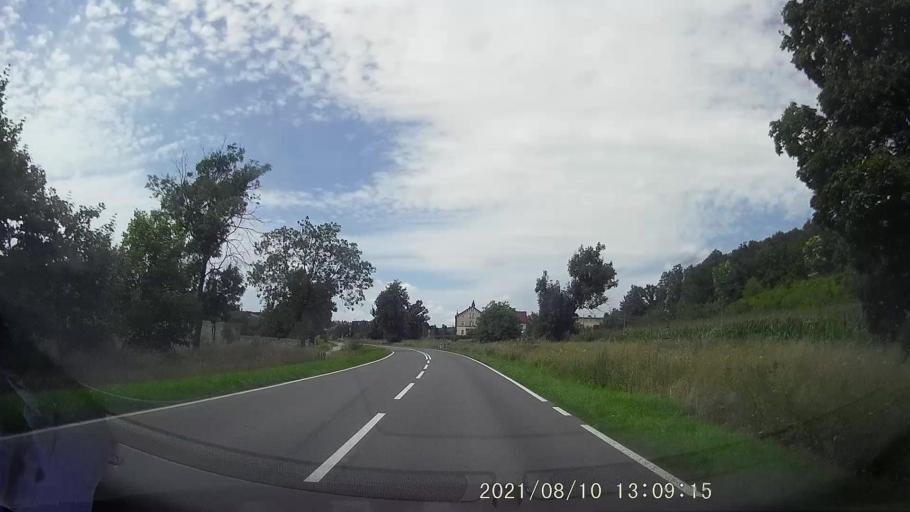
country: PL
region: Lower Silesian Voivodeship
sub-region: Powiat klodzki
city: Bozkow
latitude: 50.4972
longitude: 16.5425
